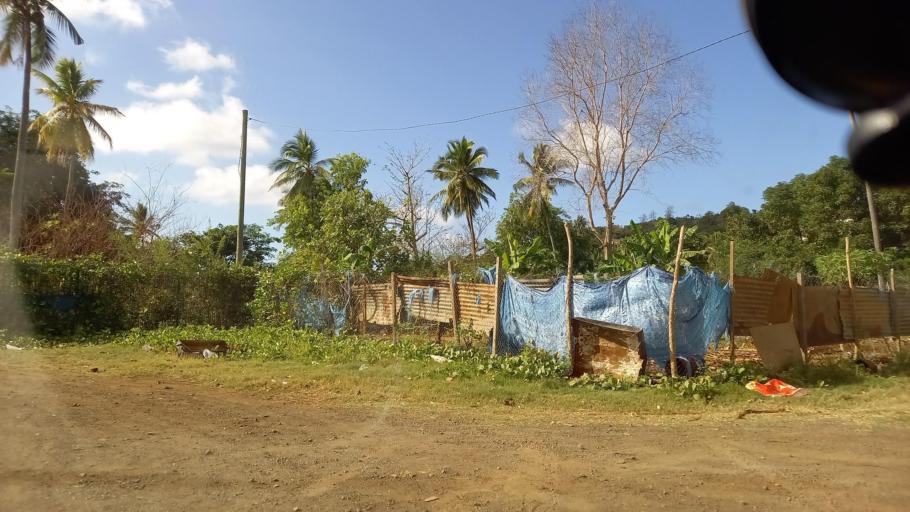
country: YT
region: Bandrele
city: Bandrele
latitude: -12.9123
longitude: 45.1955
